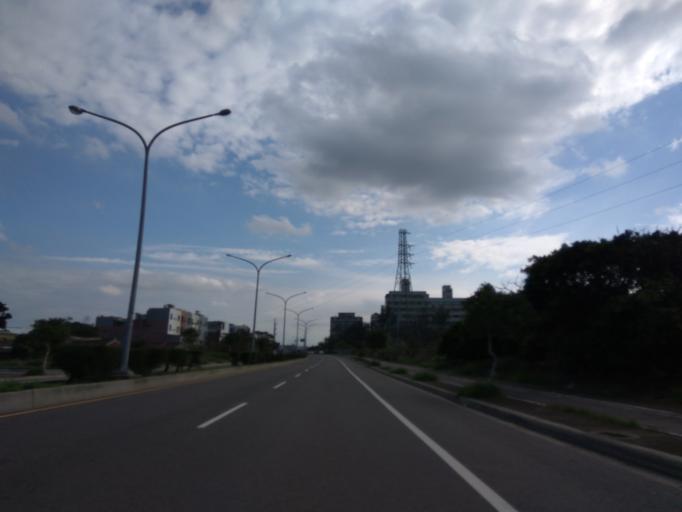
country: TW
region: Taiwan
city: Taoyuan City
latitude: 25.0661
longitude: 121.1752
